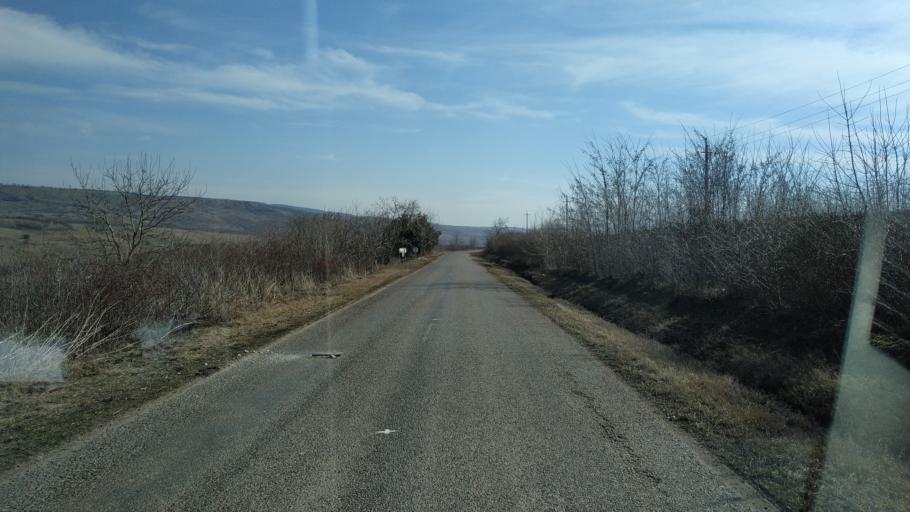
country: MD
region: Nisporeni
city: Nisporeni
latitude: 47.1782
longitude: 28.0826
